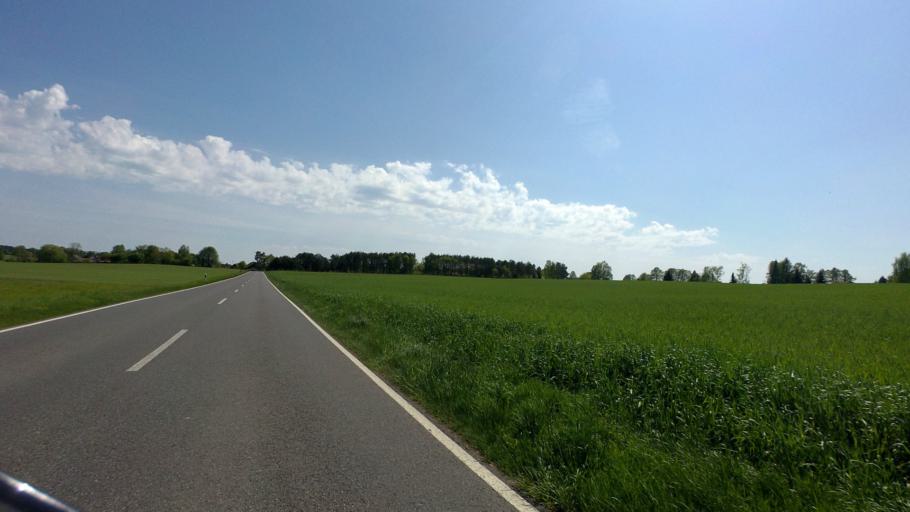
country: DE
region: Brandenburg
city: Lieberose
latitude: 51.9863
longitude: 14.2132
